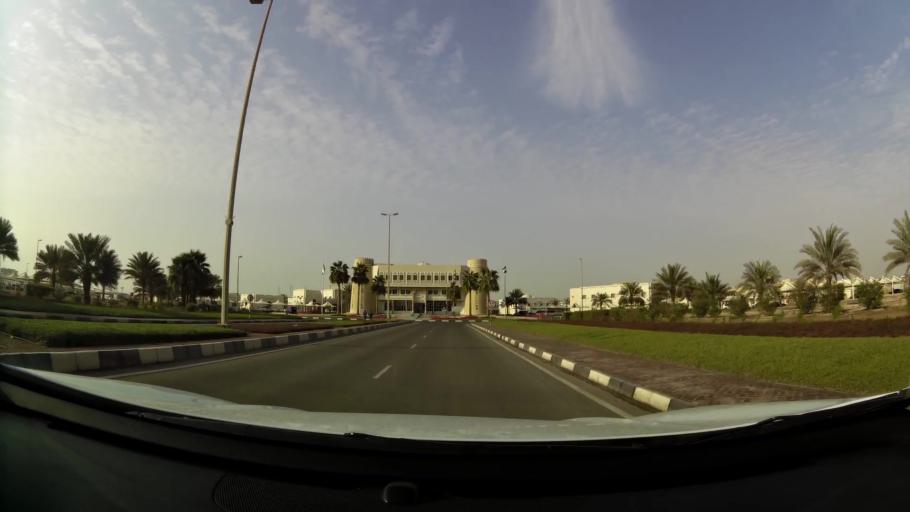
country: AE
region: Abu Dhabi
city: Abu Dhabi
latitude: 24.3265
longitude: 54.5198
